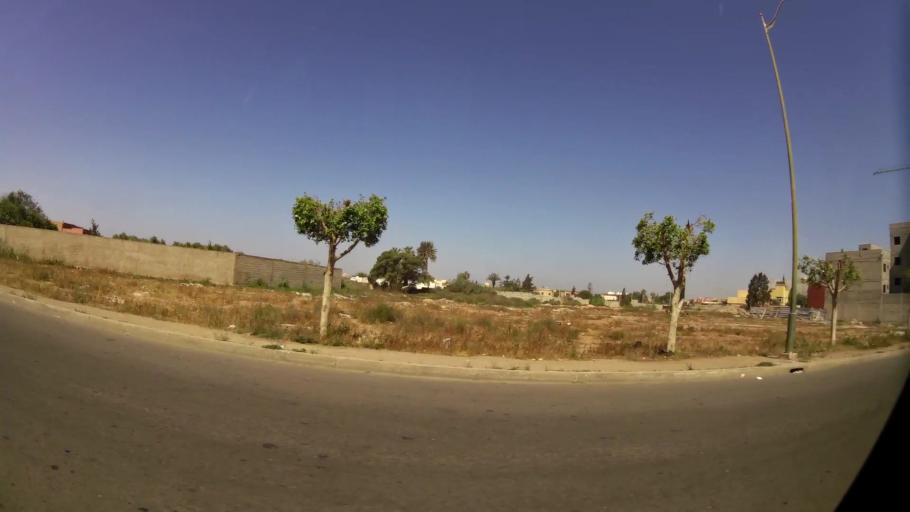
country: MA
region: Souss-Massa-Draa
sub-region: Inezgane-Ait Mellou
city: Inezgane
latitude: 30.3438
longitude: -9.5079
